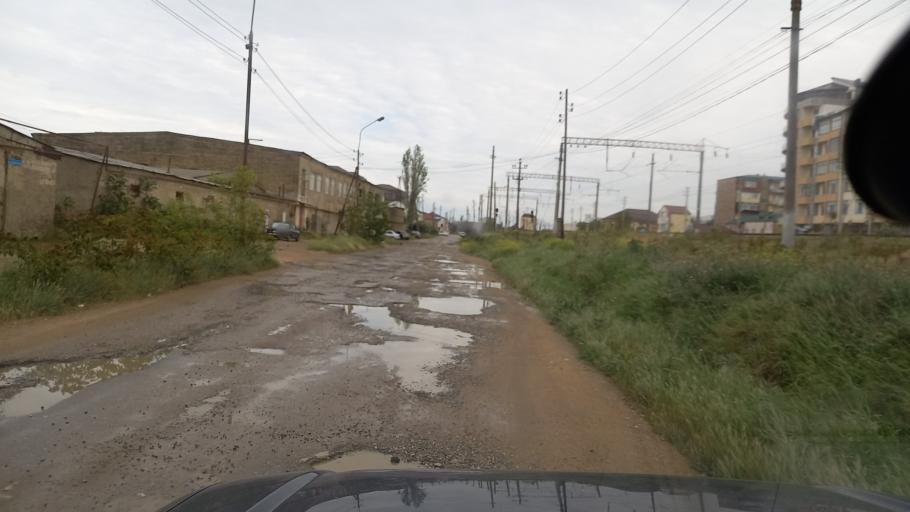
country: RU
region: Dagestan
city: Derbent
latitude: 42.0674
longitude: 48.3020
